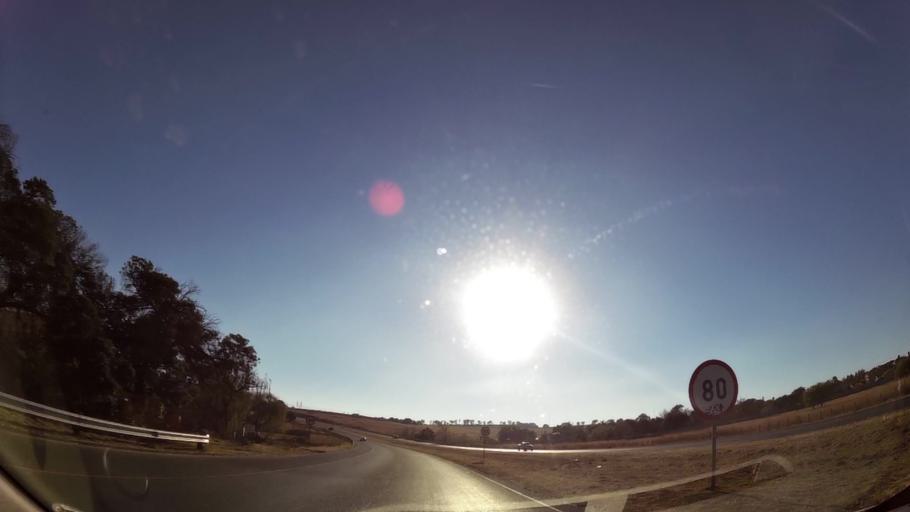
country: ZA
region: Gauteng
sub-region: City of Johannesburg Metropolitan Municipality
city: Modderfontein
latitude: -26.1002
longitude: 28.1837
